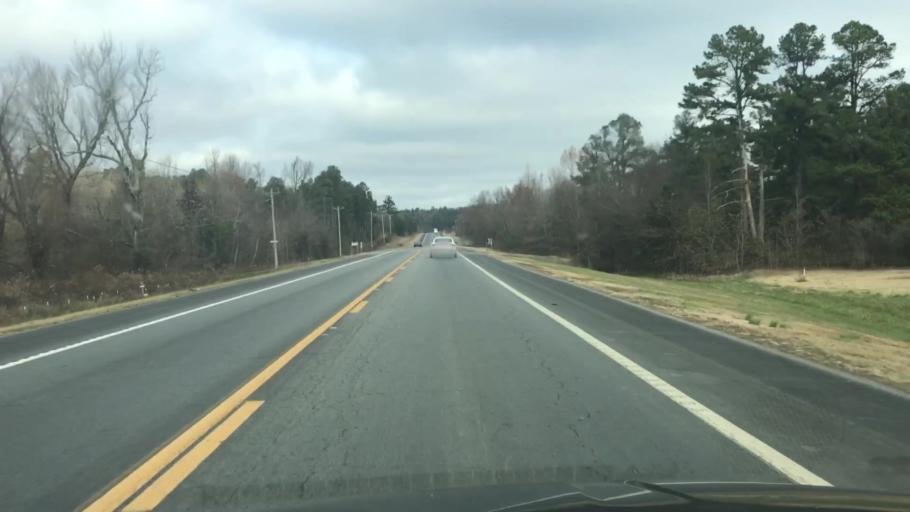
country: US
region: Arkansas
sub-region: Scott County
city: Waldron
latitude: 34.8298
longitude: -94.0408
